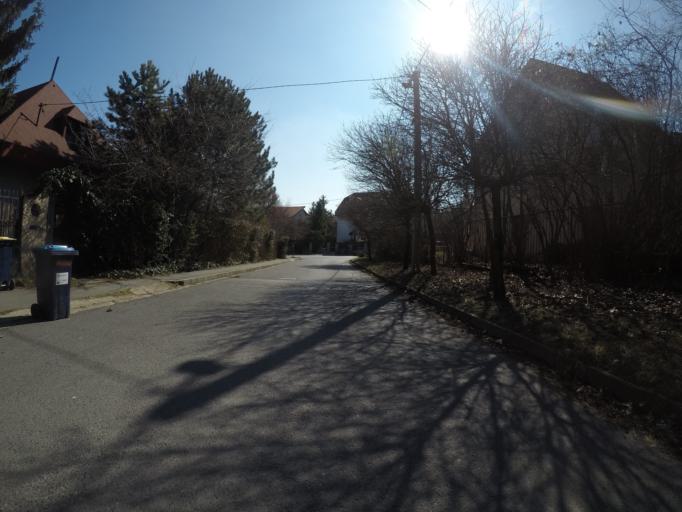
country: HU
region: Budapest
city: Budapest II. keruelet
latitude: 47.5304
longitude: 19.0060
